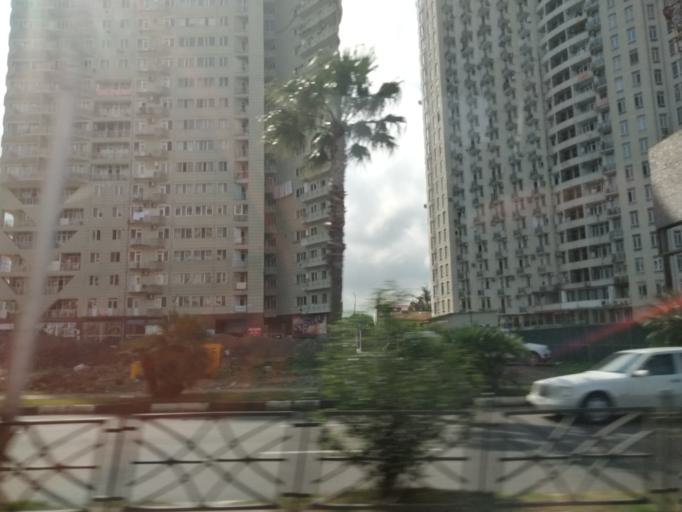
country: GE
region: Ajaria
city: Batumi
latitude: 41.6429
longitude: 41.6168
